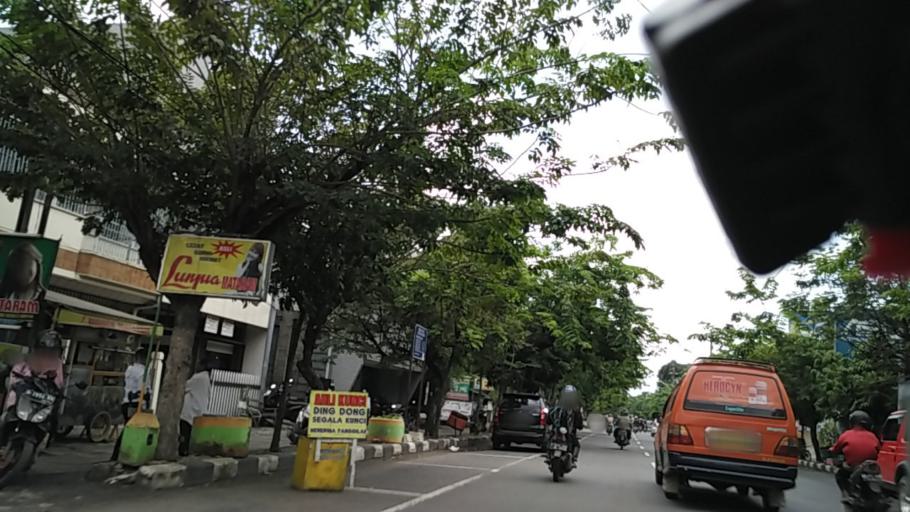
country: ID
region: Central Java
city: Semarang
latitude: -6.9927
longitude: 110.4320
